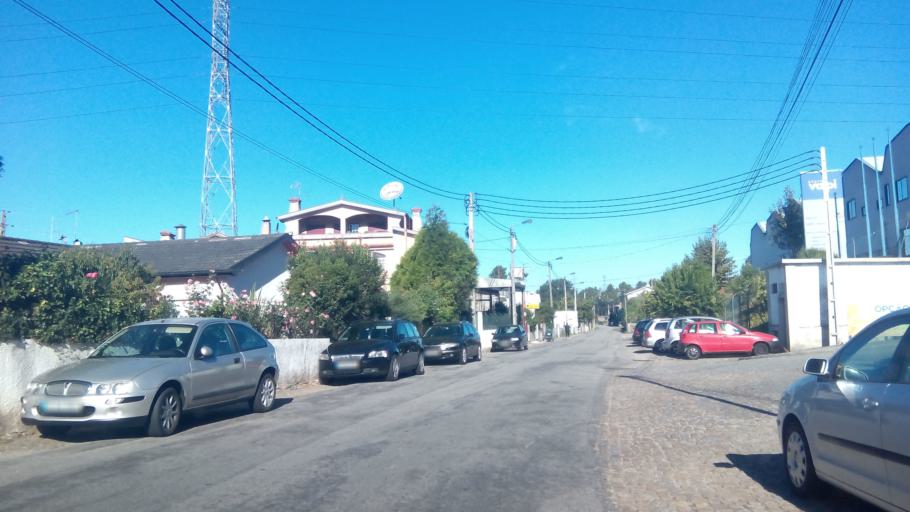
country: PT
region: Porto
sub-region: Paredes
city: Gandra
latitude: 41.1882
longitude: -8.4421
